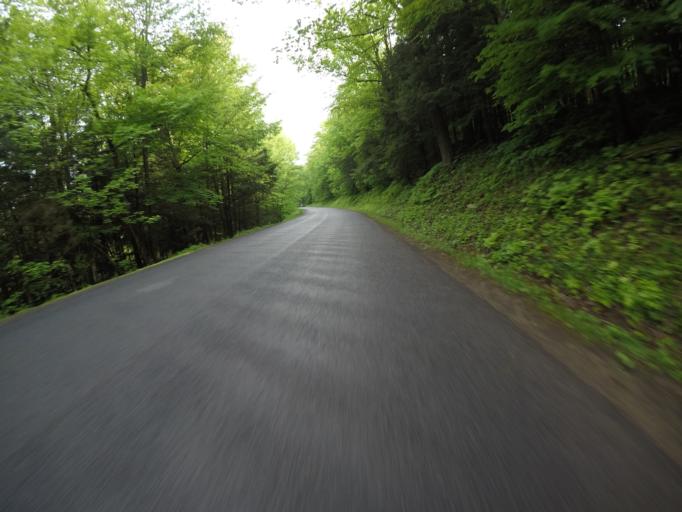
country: US
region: New York
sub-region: Delaware County
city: Stamford
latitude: 42.1724
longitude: -74.6671
